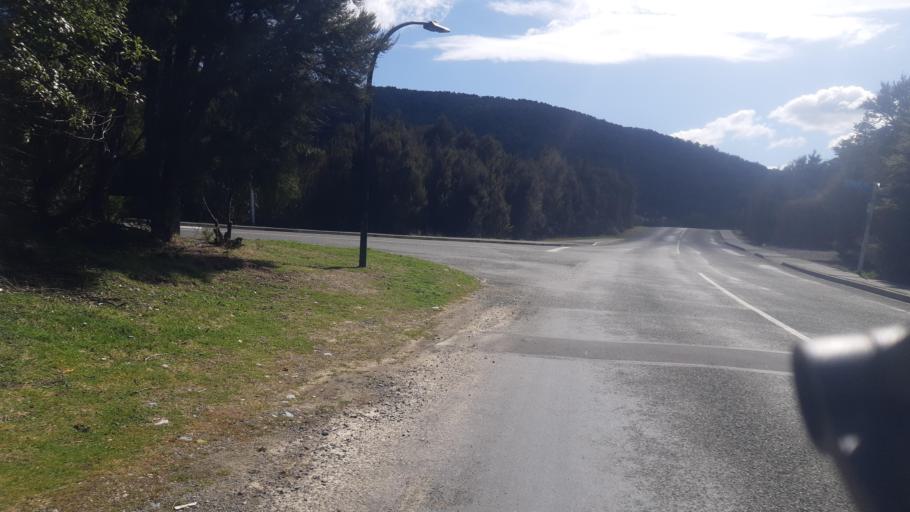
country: NZ
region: Tasman
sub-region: Tasman District
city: Wakefield
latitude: -41.8045
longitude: 172.8443
